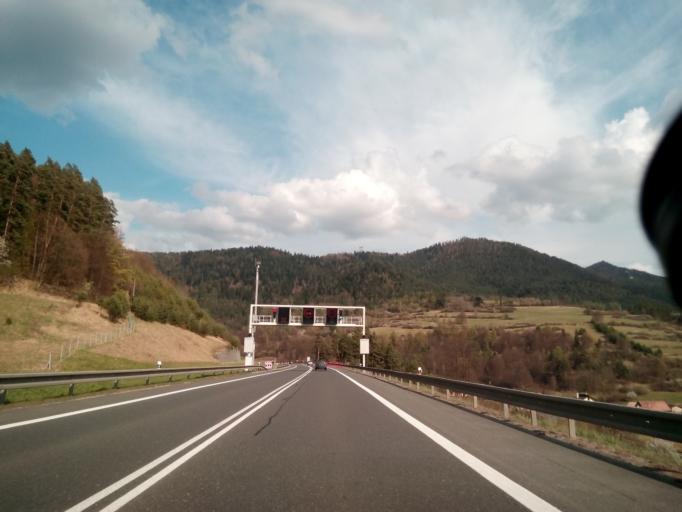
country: SK
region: Presovsky
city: Spisske Podhradie
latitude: 49.0093
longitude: 20.8312
